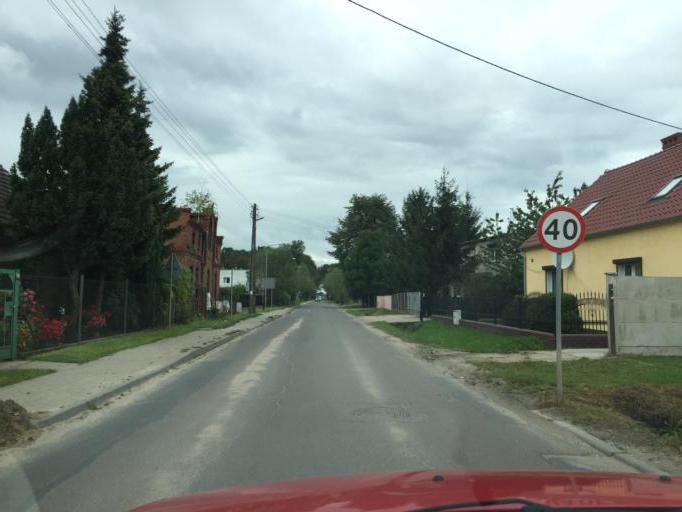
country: PL
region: Greater Poland Voivodeship
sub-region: Powiat poznanski
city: Plewiska
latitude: 52.3668
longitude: 16.8094
